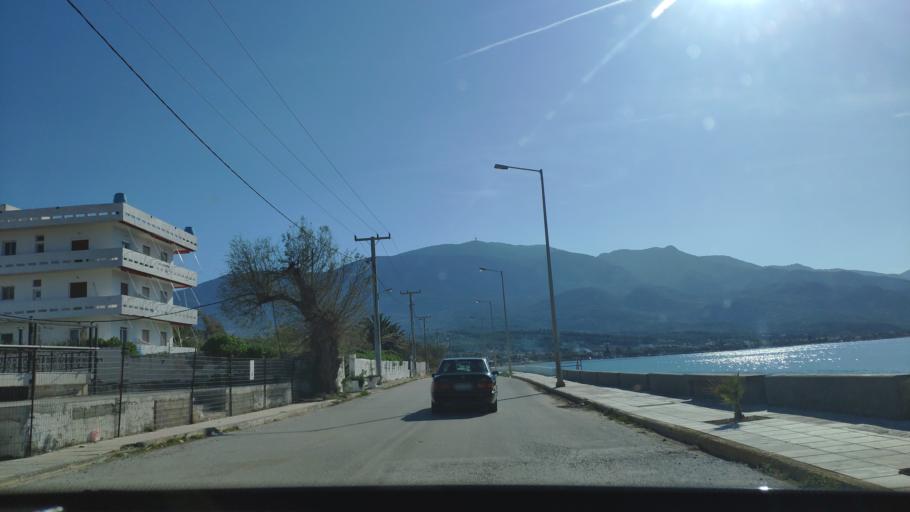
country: GR
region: Attica
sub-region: Nomarchia Dytikis Attikis
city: Kineta
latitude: 38.0809
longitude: 23.1763
